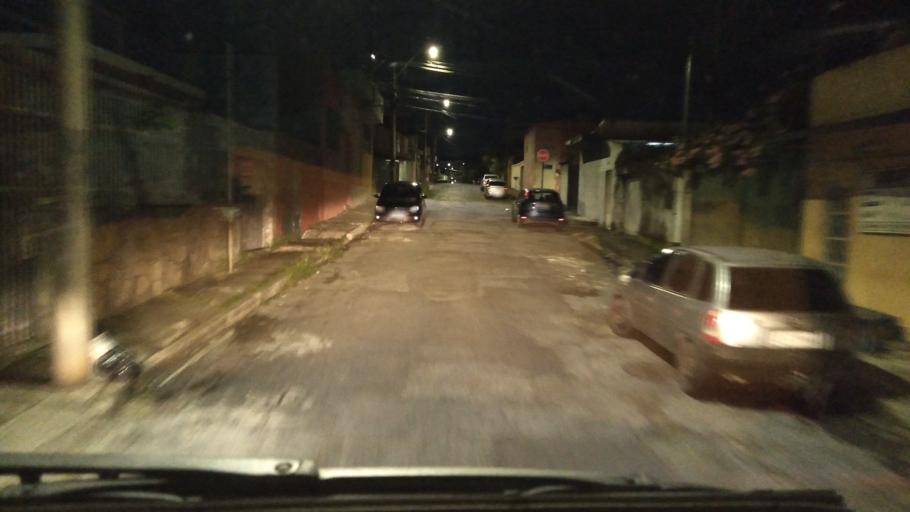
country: BR
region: Minas Gerais
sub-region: Belo Horizonte
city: Belo Horizonte
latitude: -19.8983
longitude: -43.9705
